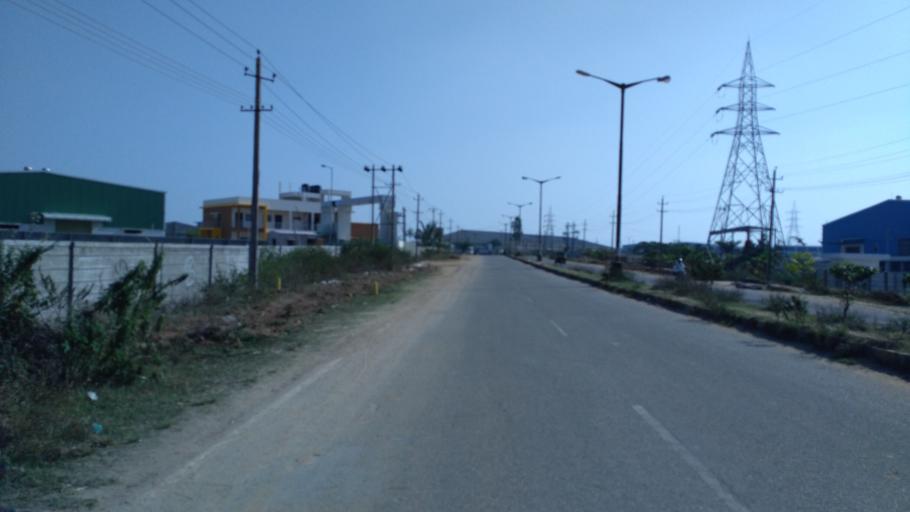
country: IN
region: Karnataka
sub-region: Hassan
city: Hassan
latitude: 12.9792
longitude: 76.1206
